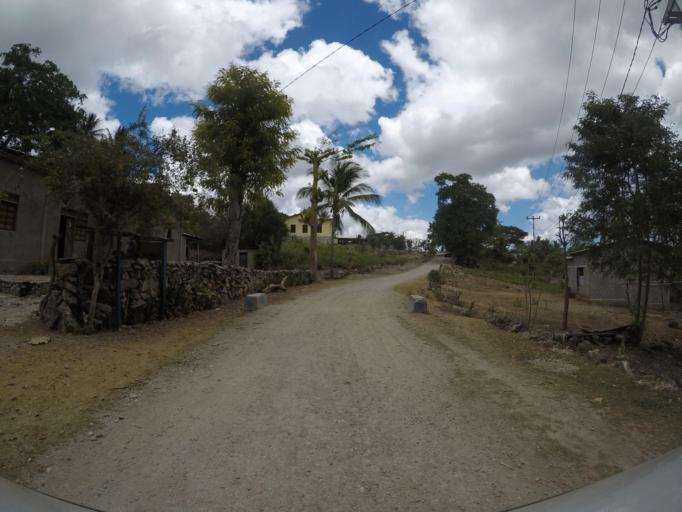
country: TL
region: Lautem
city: Lospalos
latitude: -8.3814
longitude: 126.9217
